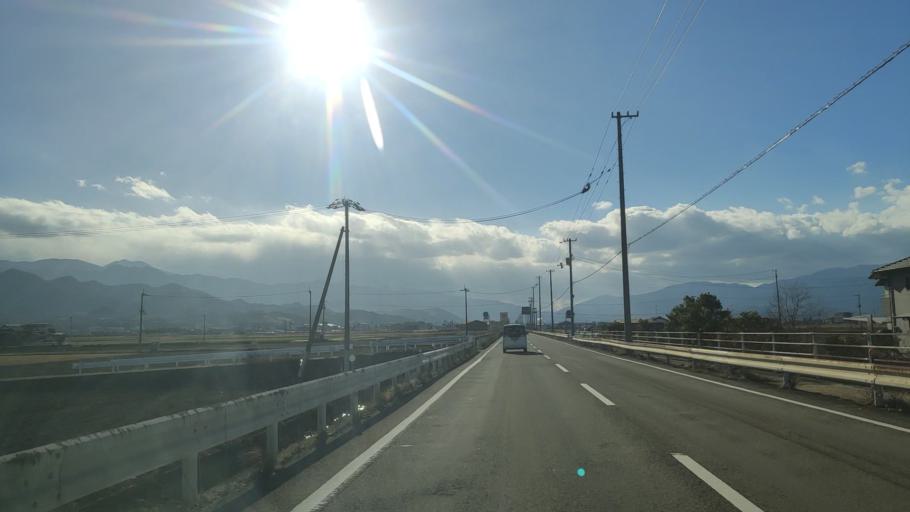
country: JP
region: Ehime
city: Saijo
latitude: 33.9179
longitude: 133.1227
